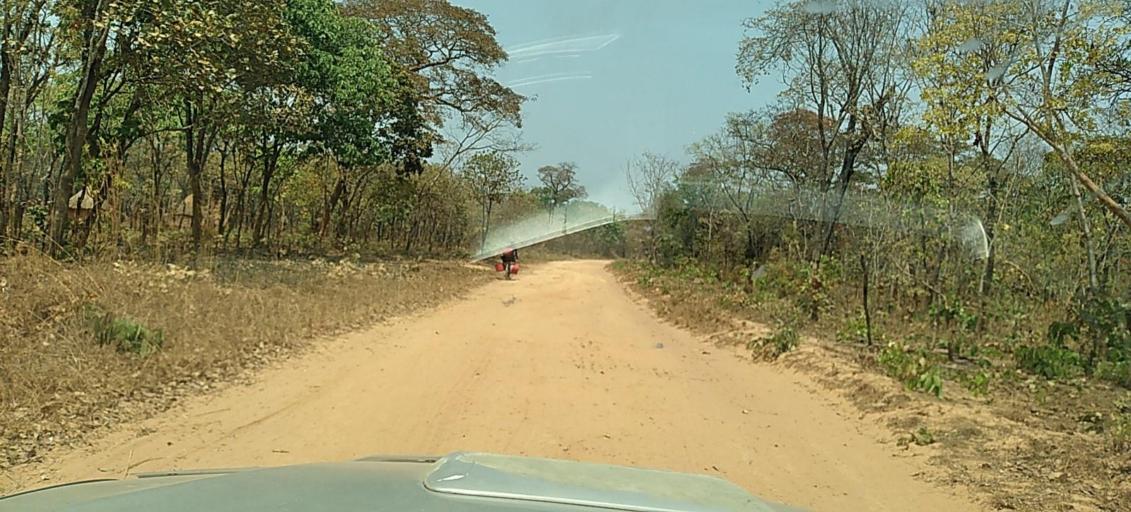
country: ZM
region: North-Western
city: Kasempa
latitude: -13.6550
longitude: 26.2584
